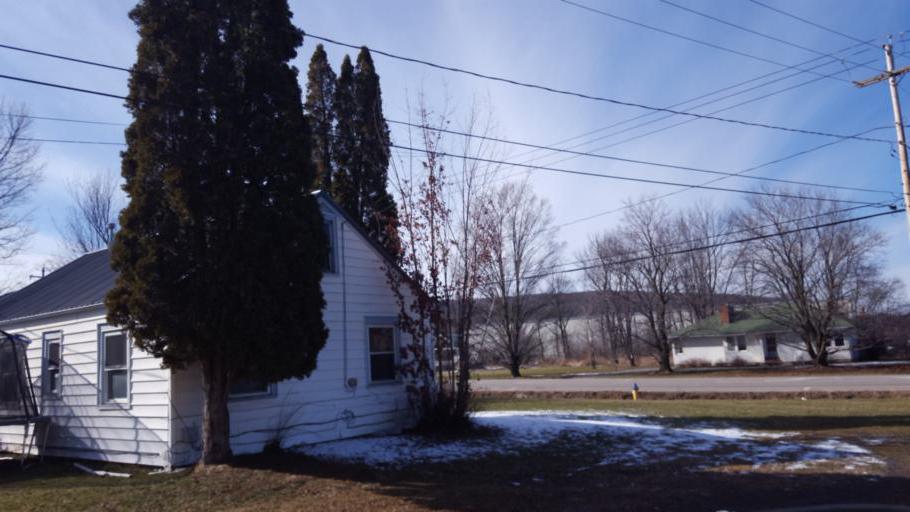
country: US
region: New York
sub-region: Allegany County
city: Wellsville
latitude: 42.1252
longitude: -77.9711
